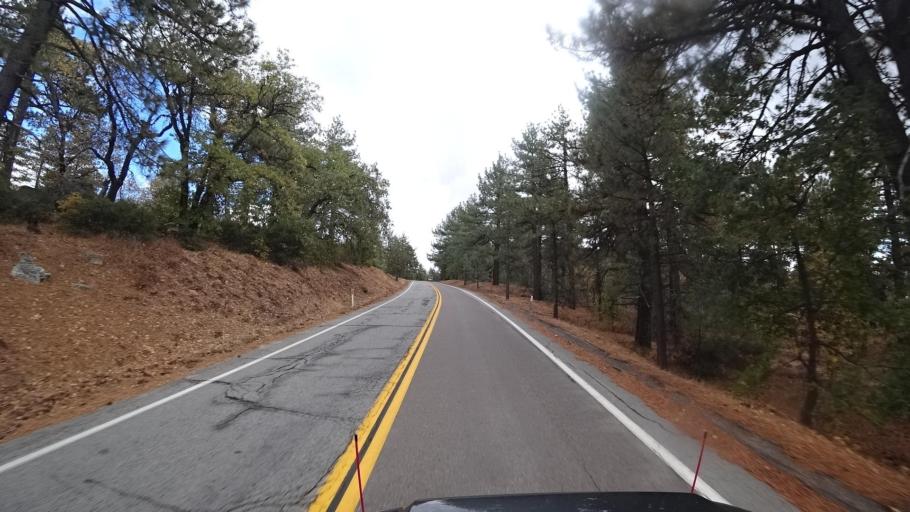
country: US
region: California
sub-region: San Diego County
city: Pine Valley
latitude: 32.8530
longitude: -116.4532
